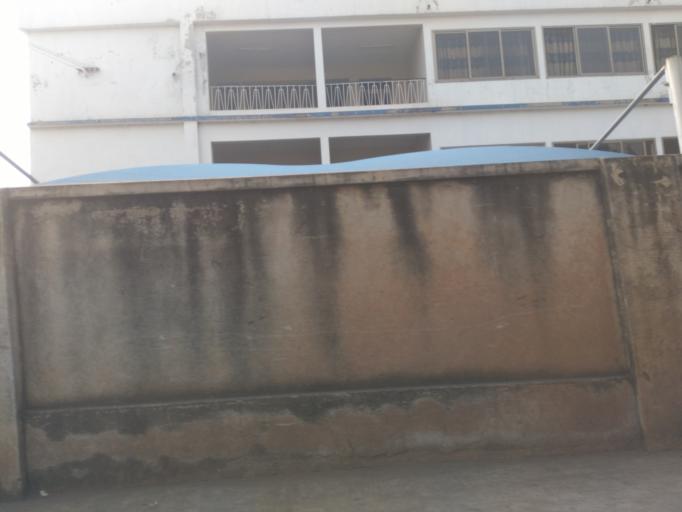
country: GH
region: Ashanti
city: Kumasi
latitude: 6.6950
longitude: -1.6187
